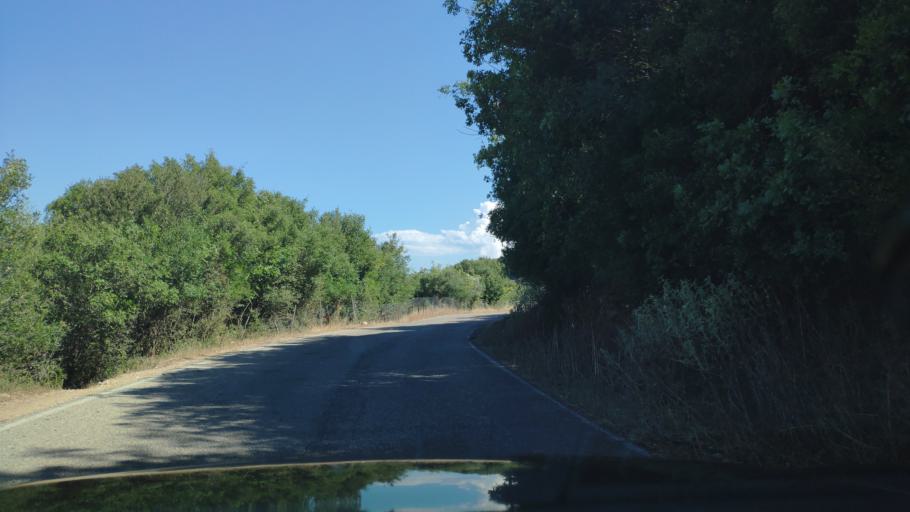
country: GR
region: West Greece
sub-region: Nomos Aitolias kai Akarnanias
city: Katouna
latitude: 38.8288
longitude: 21.0991
